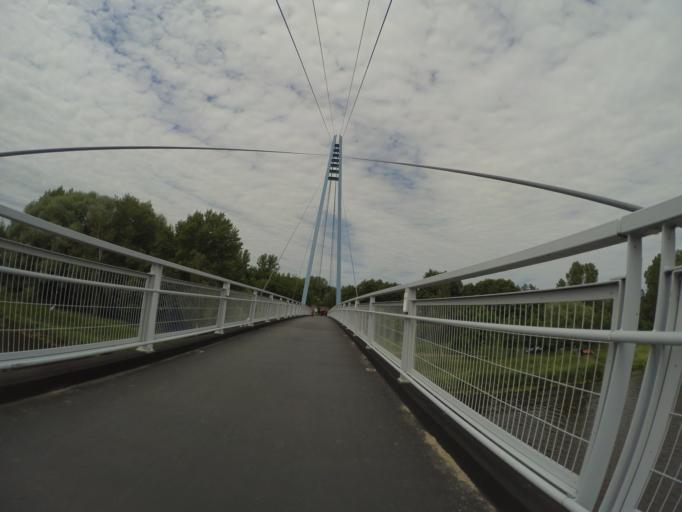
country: CZ
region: Central Bohemia
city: Celakovice
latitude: 50.1706
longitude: 14.7584
